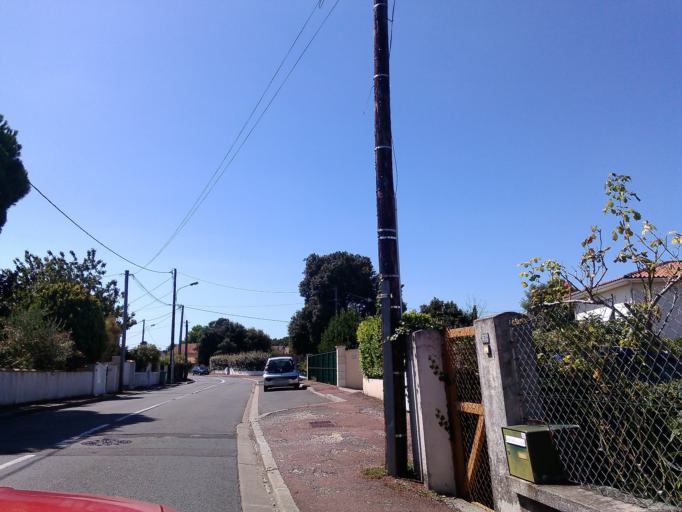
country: FR
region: Poitou-Charentes
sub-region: Departement de la Charente-Maritime
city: Vaux-sur-Mer
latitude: 45.6402
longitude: -1.0678
